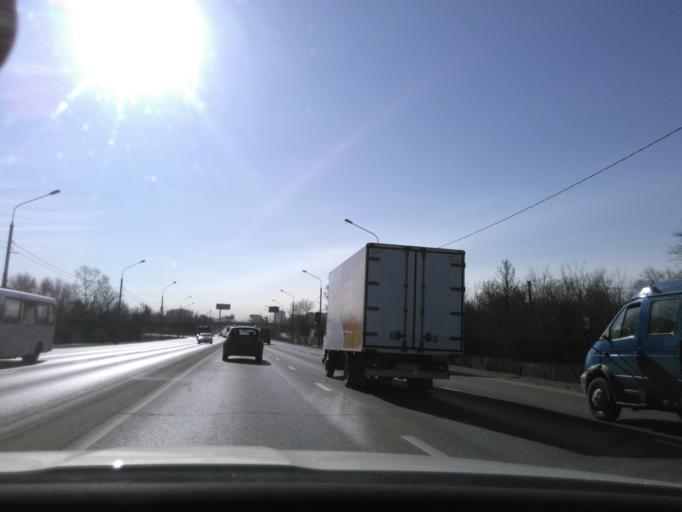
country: RU
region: Moskovskaya
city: Novopodrezkovo
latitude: 55.9237
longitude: 37.3885
